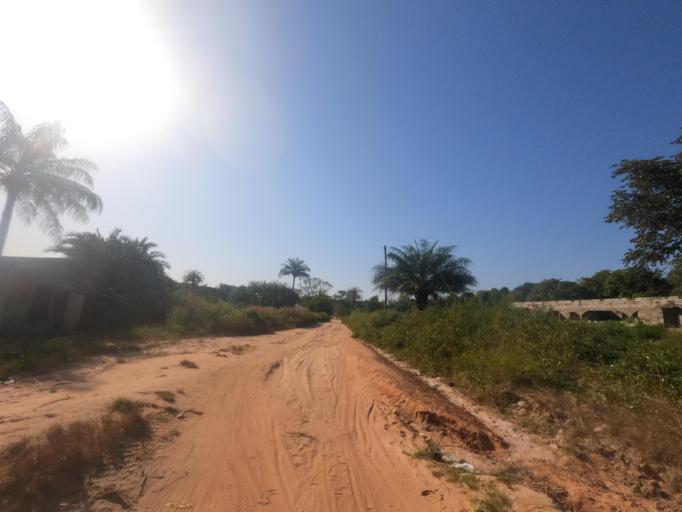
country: GW
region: Cacheu
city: Cacheu
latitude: 12.4012
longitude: -16.2008
